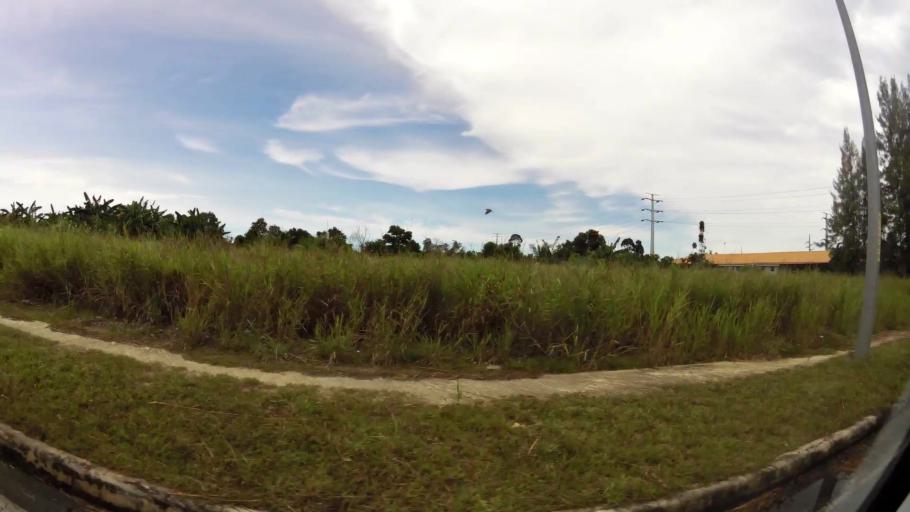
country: BN
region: Belait
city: Kuala Belait
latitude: 4.5843
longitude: 114.2605
